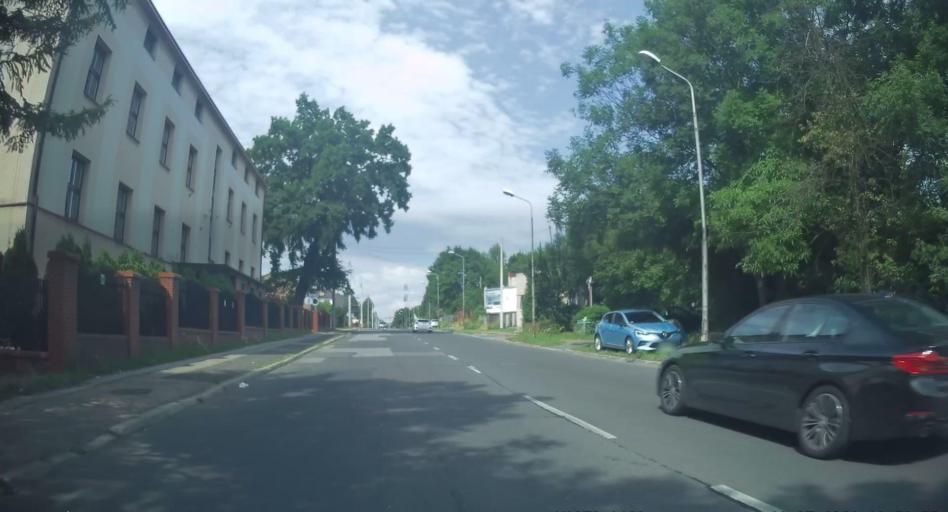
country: PL
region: Silesian Voivodeship
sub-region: Czestochowa
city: Czestochowa
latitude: 50.8092
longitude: 19.0826
